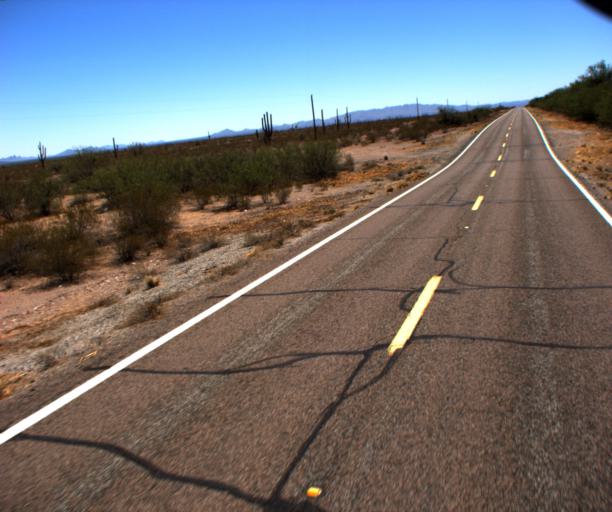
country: US
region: Arizona
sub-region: Pima County
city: Ajo
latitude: 32.2038
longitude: -112.5254
